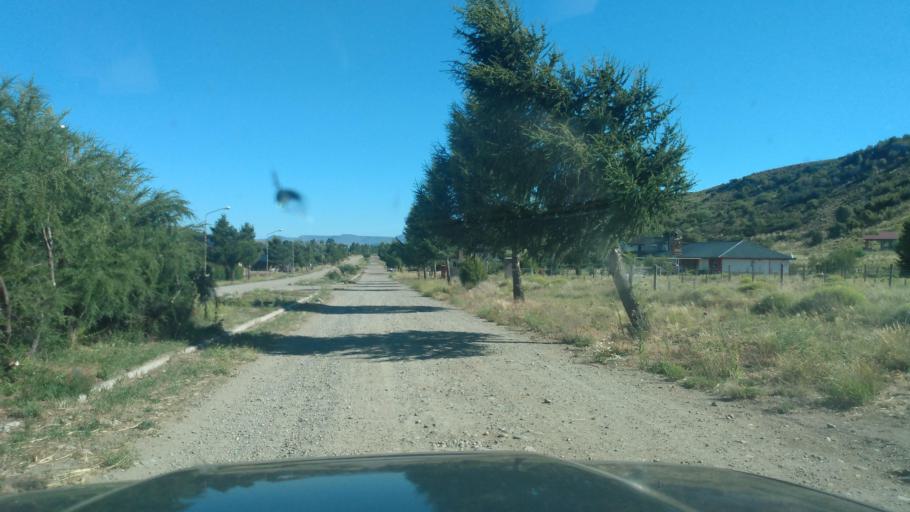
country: AR
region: Neuquen
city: Junin de los Andes
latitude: -39.9650
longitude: -71.0830
